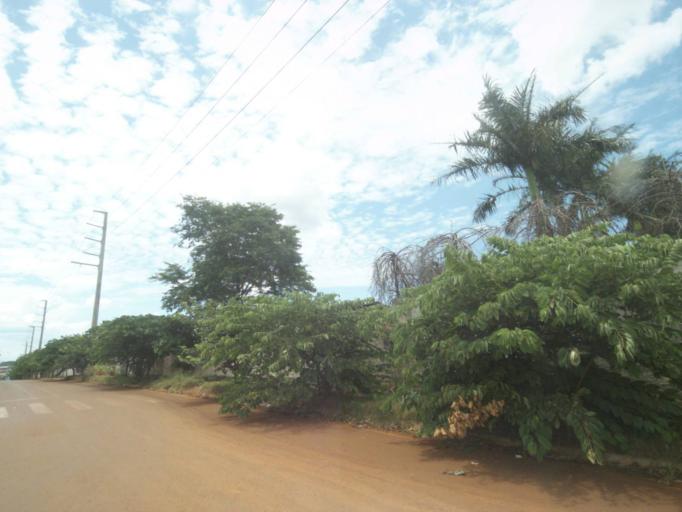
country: BR
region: Parana
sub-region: Londrina
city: Londrina
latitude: -23.3233
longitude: -51.1882
